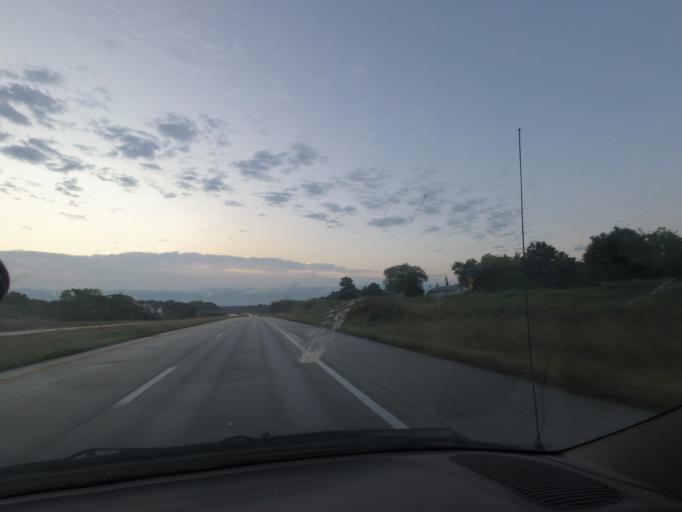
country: US
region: Missouri
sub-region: Macon County
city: Macon
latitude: 39.7526
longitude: -92.5336
